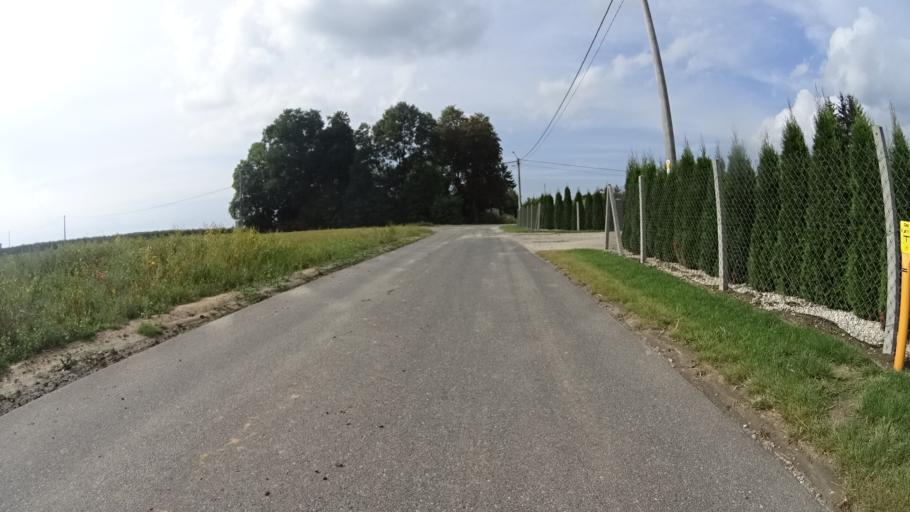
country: PL
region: Masovian Voivodeship
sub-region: Powiat grojecki
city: Goszczyn
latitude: 51.7094
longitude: 20.8413
